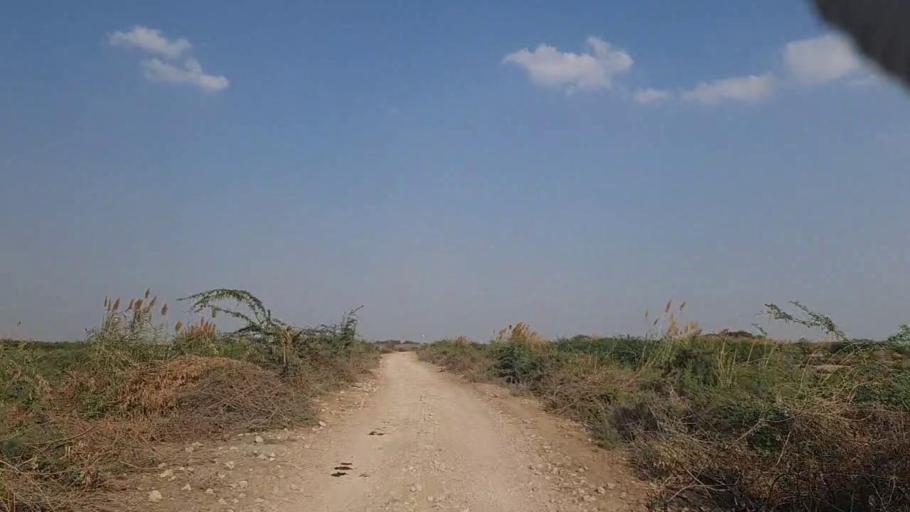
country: PK
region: Sindh
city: Jati
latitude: 24.4297
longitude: 68.3706
